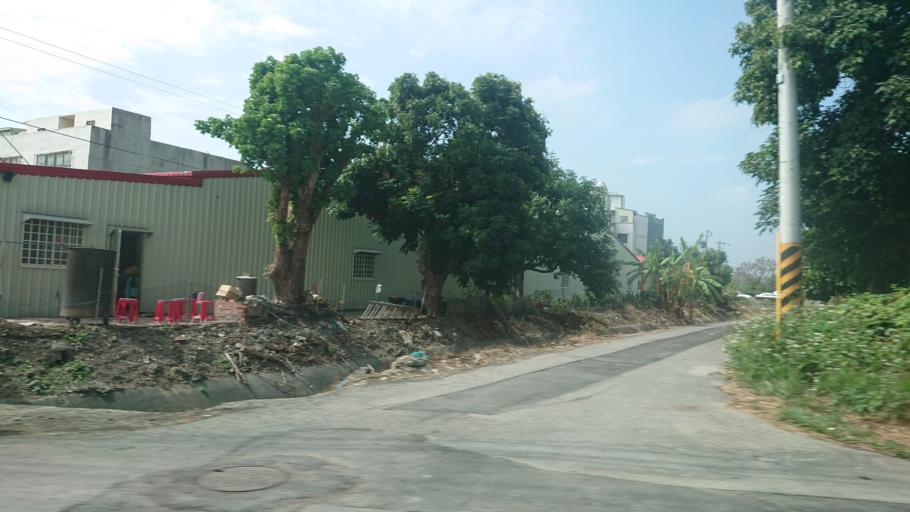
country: TW
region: Taiwan
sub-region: Chiayi
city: Taibao
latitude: 23.4715
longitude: 120.2445
